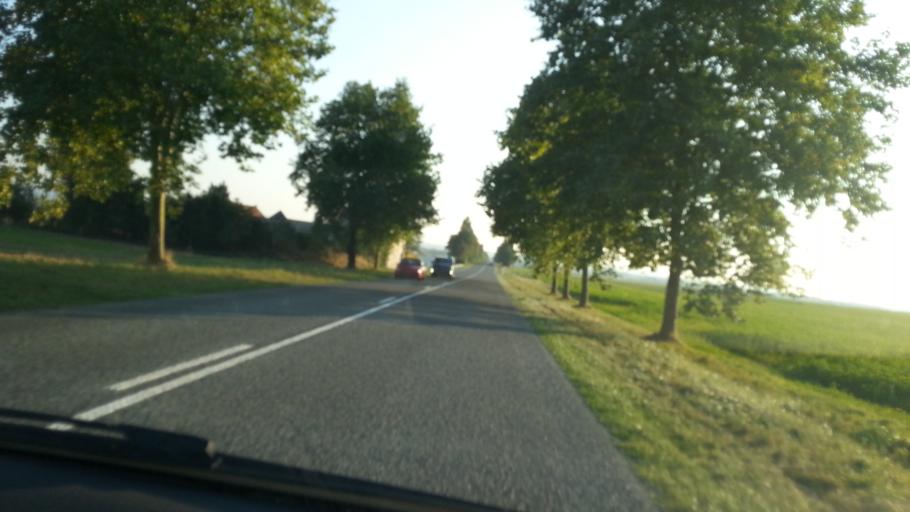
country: FR
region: Picardie
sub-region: Departement de l'Oise
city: Saint-Martin-Longueau
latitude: 49.3628
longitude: 2.6131
